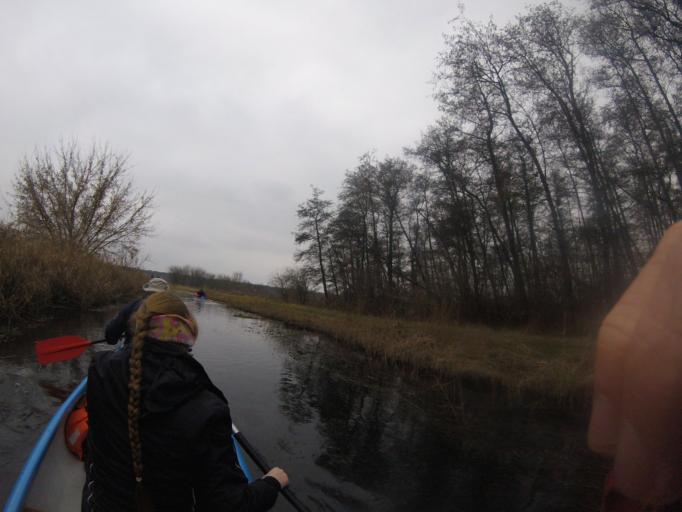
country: HU
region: Zala
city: Heviz
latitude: 46.7659
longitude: 17.2078
